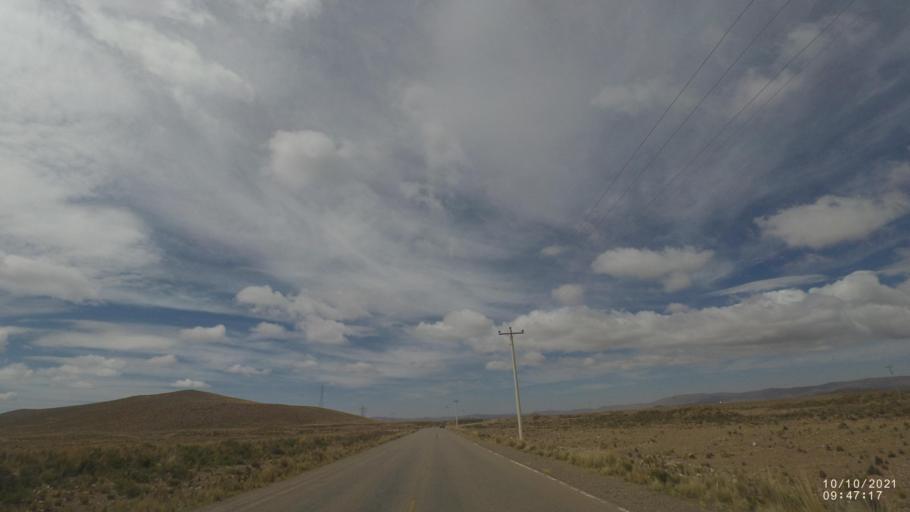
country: BO
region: La Paz
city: Quime
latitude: -17.1918
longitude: -67.3407
